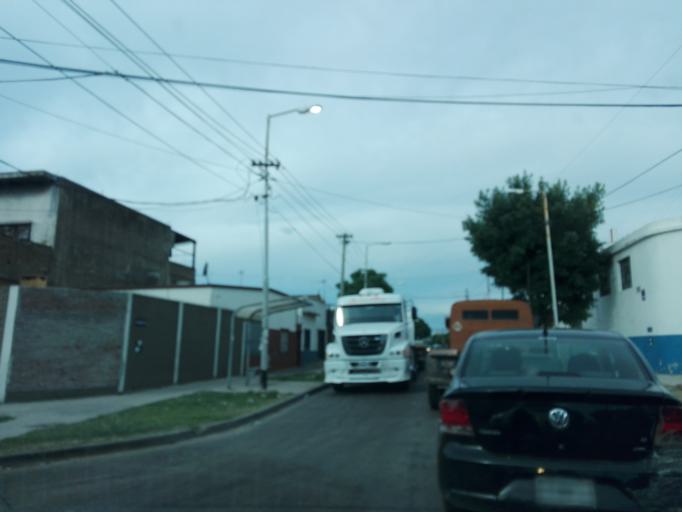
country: AR
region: Buenos Aires
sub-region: Partido de Avellaneda
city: Avellaneda
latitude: -34.6931
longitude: -58.3565
